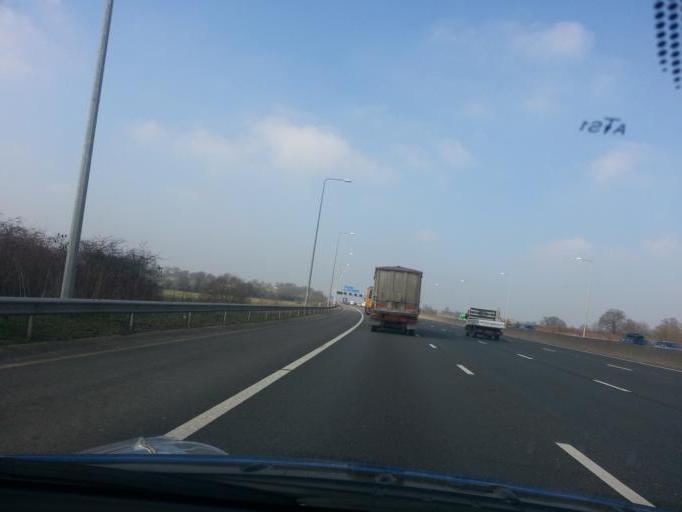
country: GB
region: England
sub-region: Hertfordshire
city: Shenley AV
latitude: 51.7018
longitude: -0.2455
